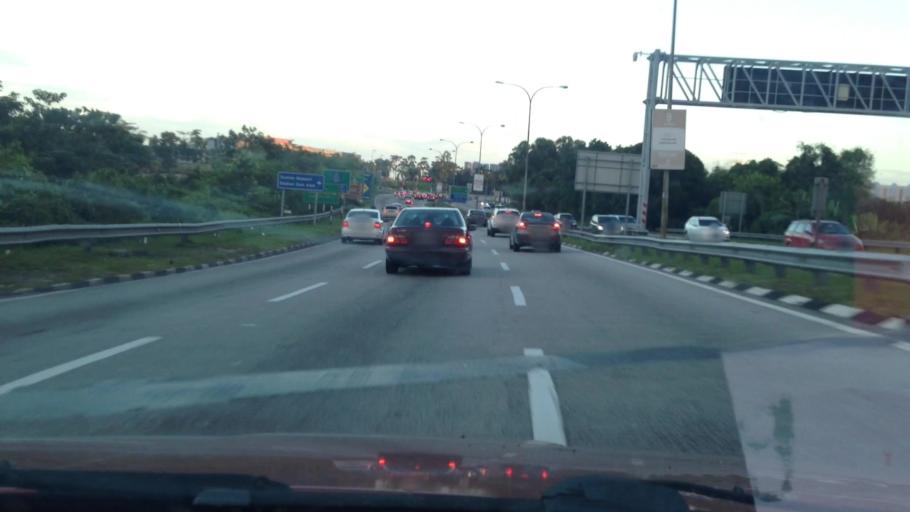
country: MY
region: Selangor
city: Shah Alam
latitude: 3.0907
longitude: 101.5510
